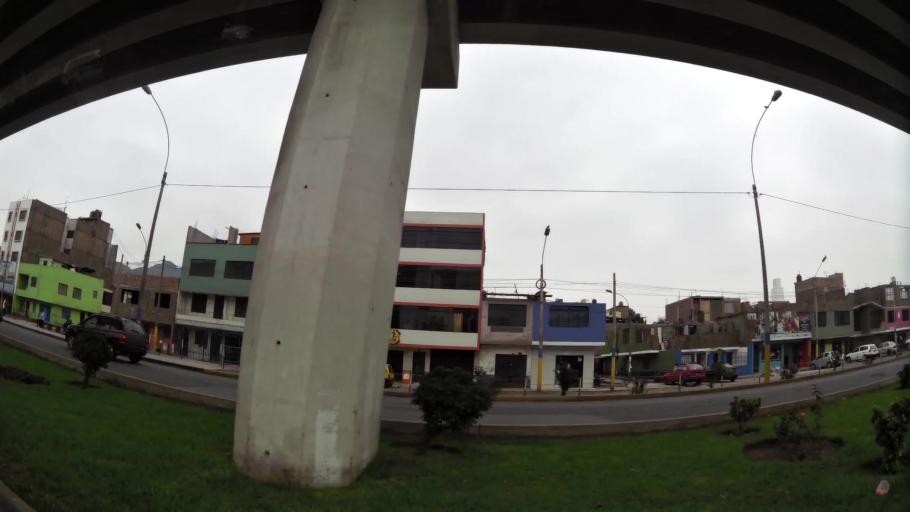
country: PE
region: Lima
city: Lima
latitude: -12.0214
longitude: -77.0060
